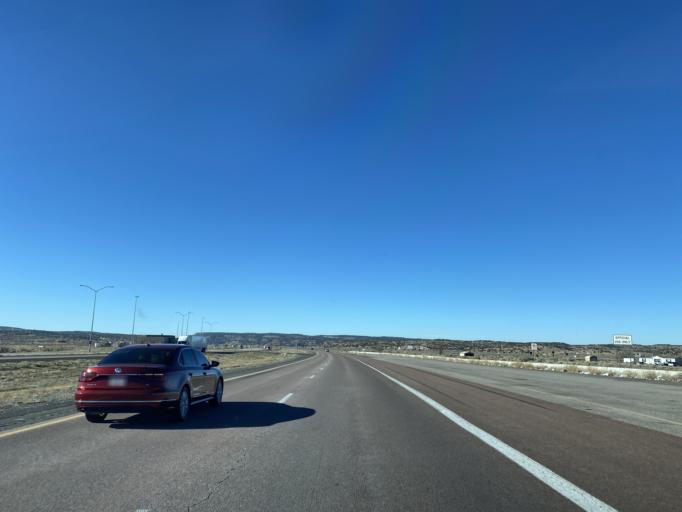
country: US
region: New Mexico
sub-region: McKinley County
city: Gallup
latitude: 35.4879
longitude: -108.8974
